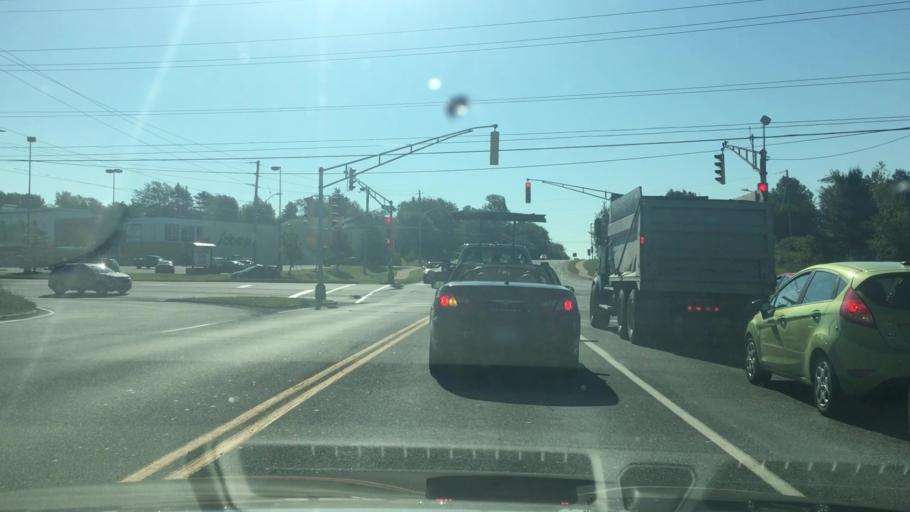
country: CA
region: Nova Scotia
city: Cole Harbour
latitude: 44.6942
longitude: -63.4994
